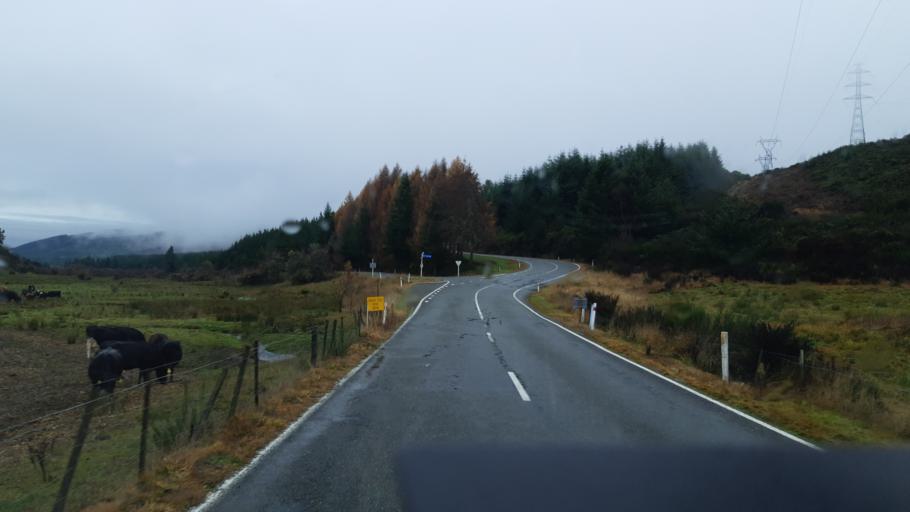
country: NZ
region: Tasman
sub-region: Tasman District
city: Wakefield
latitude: -41.6685
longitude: 172.8742
